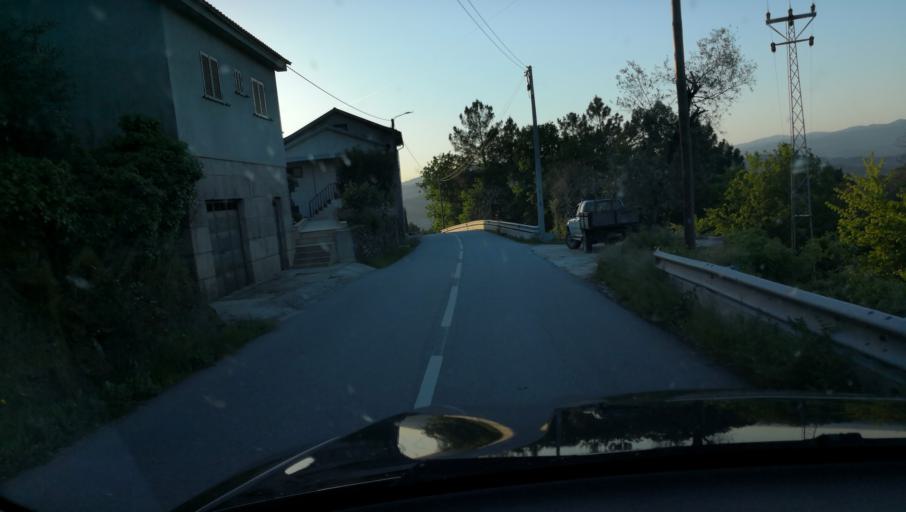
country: PT
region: Vila Real
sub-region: Mondim de Basto
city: Mondim de Basto
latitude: 41.4108
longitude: -7.9332
